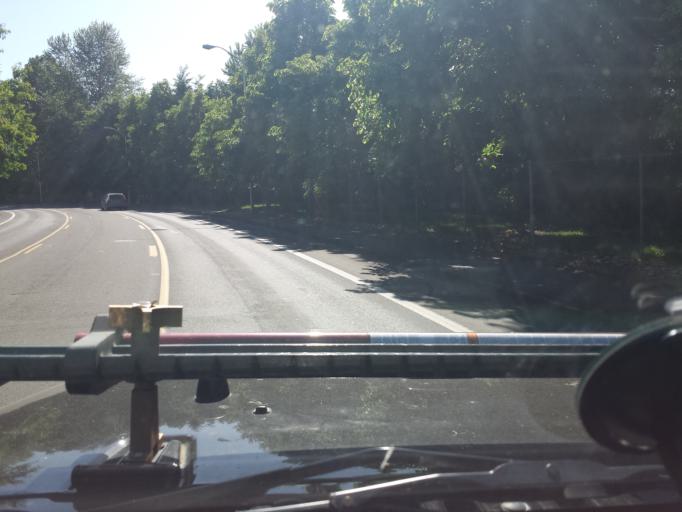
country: US
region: Washington
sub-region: Clark County
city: Walnut Grove
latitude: 45.6516
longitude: -122.5967
